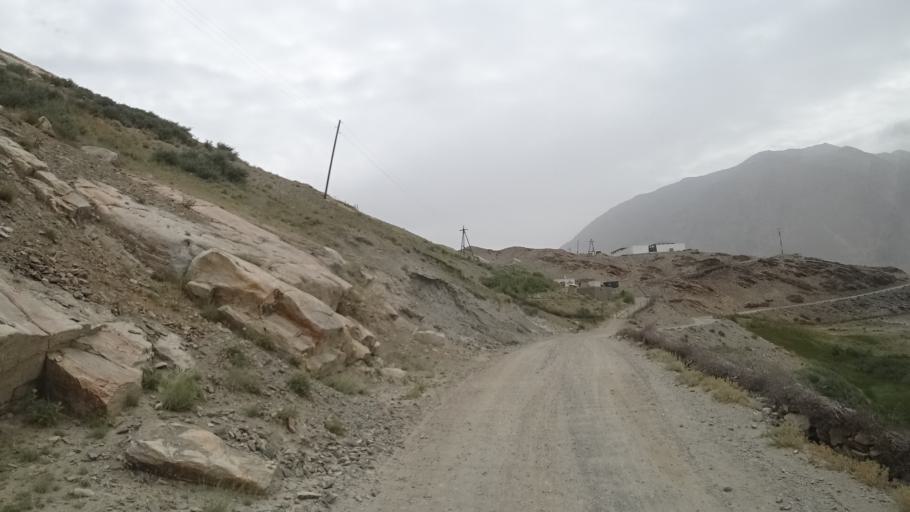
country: AF
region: Badakhshan
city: Khandud
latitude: 37.0050
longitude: 72.5449
